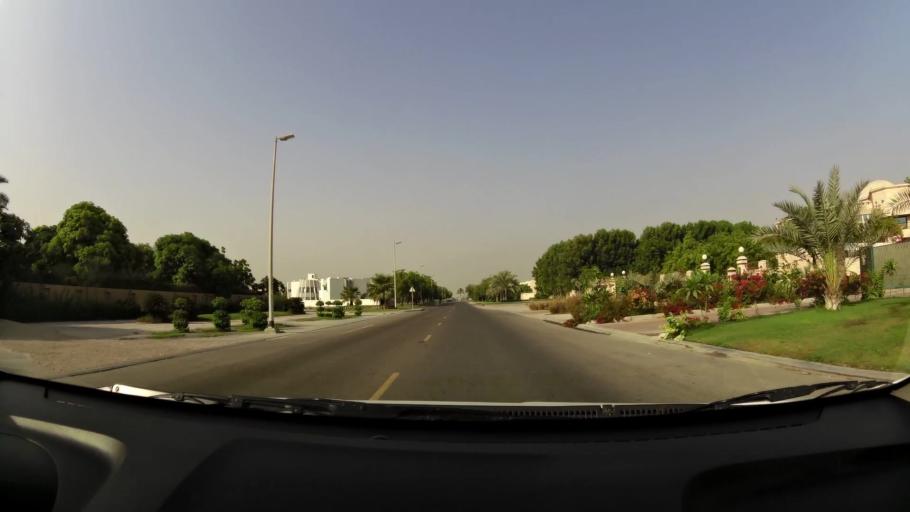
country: AE
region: Ash Shariqah
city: Sharjah
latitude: 25.3113
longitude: 55.3424
